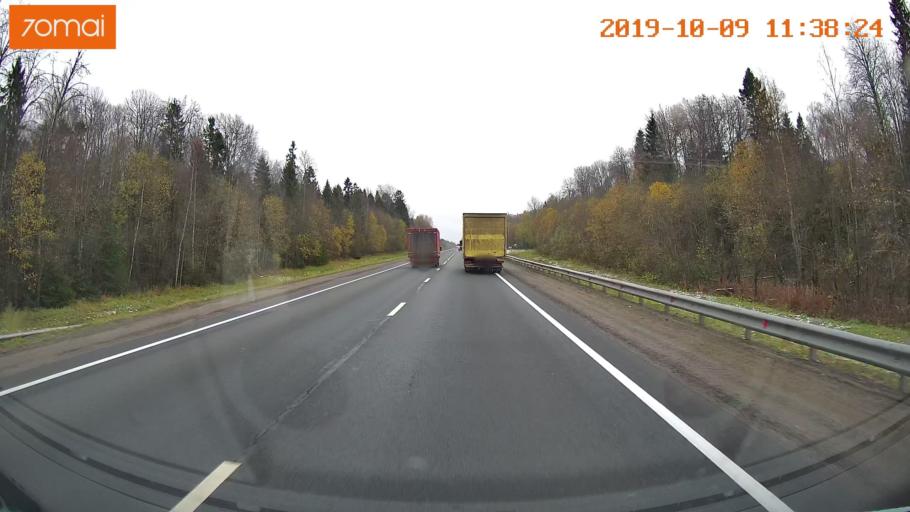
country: RU
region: Vologda
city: Gryazovets
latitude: 58.9686
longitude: 40.1554
